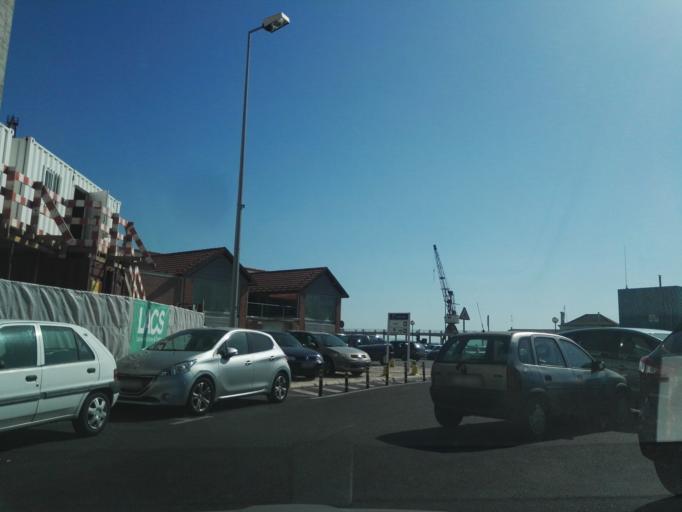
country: PT
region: Setubal
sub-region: Almada
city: Cacilhas
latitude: 38.7029
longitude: -9.1620
